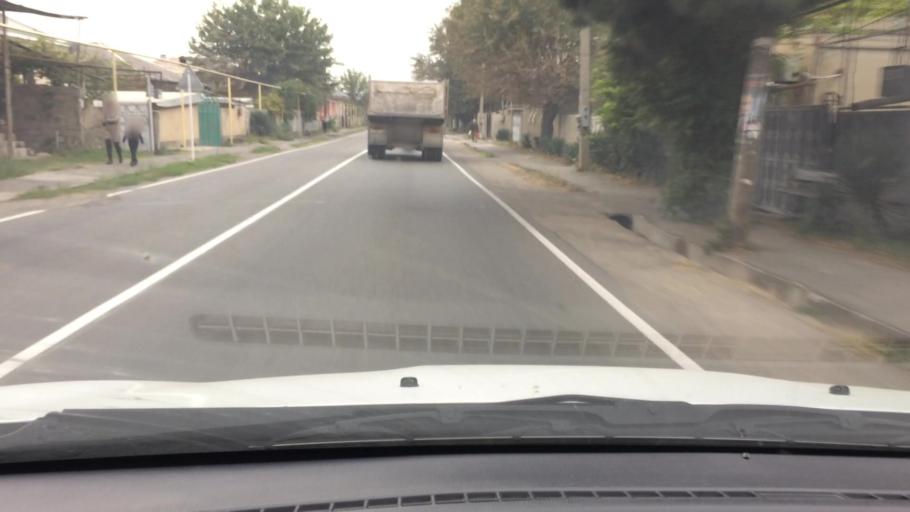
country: GE
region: Kvemo Kartli
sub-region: Marneuli
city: Marneuli
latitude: 41.4827
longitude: 44.8011
